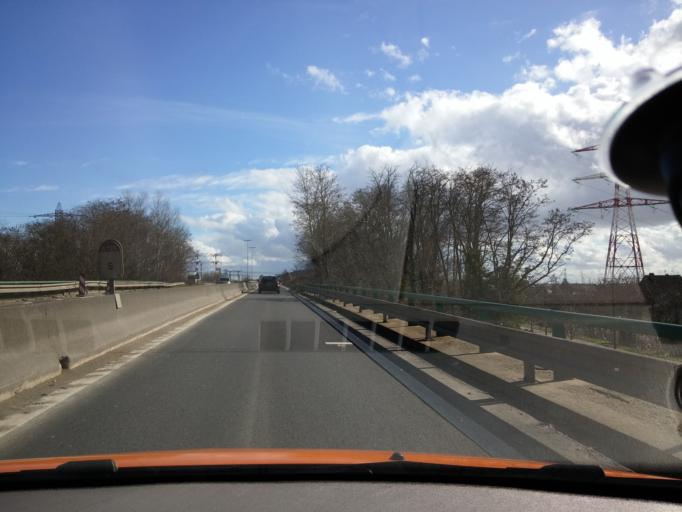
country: FR
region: Ile-de-France
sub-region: Departement de l'Essonne
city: Palaiseau
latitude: 48.7211
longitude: 2.2526
